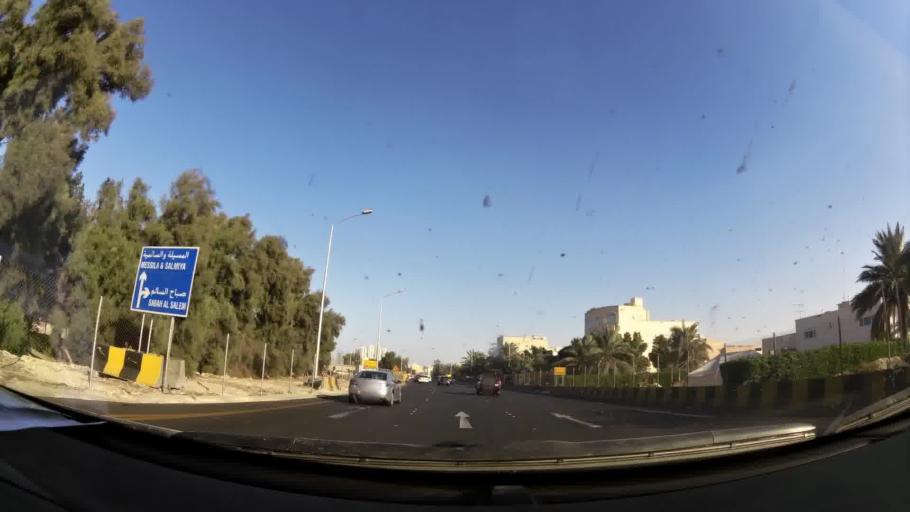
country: KW
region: Mubarak al Kabir
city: Sabah as Salim
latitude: 29.2638
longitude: 48.0614
